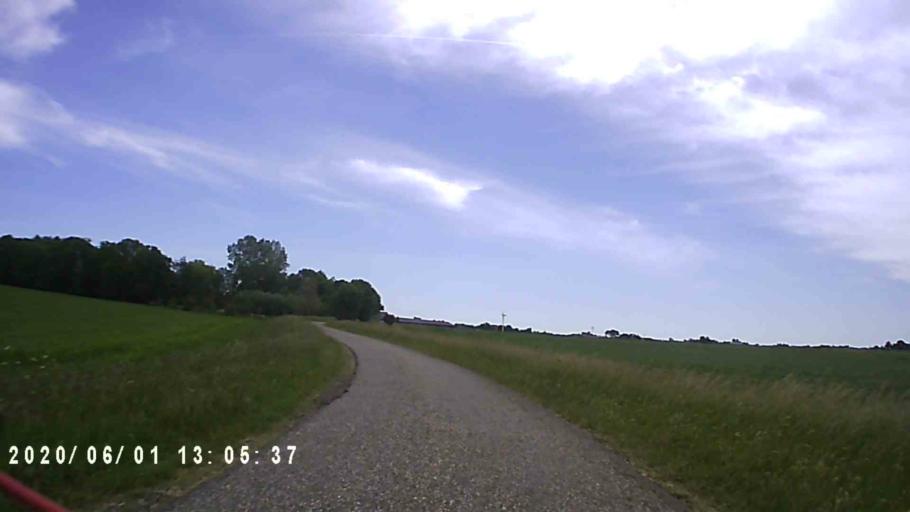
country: NL
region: Friesland
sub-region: Gemeente Franekeradeel
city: Tzum
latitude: 53.1365
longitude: 5.5483
